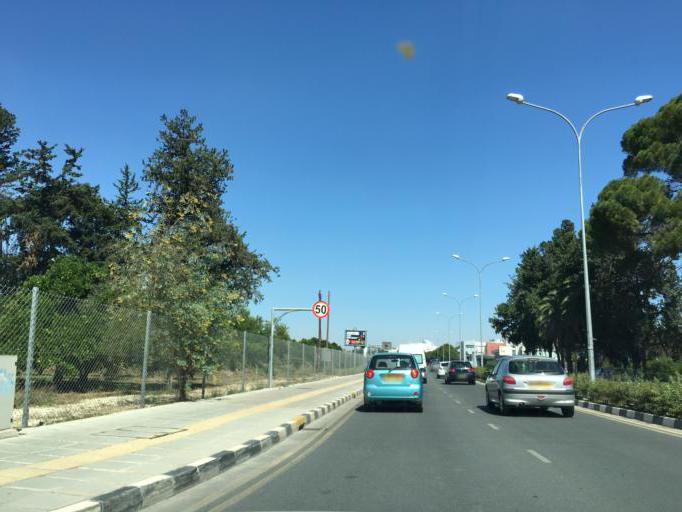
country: CY
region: Lefkosia
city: Nicosia
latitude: 35.1612
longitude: 33.3384
